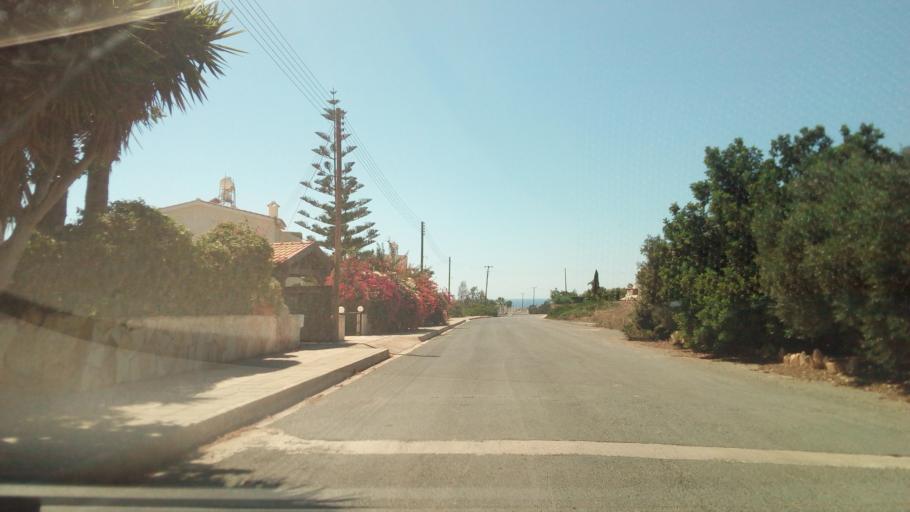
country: CY
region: Pafos
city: Pegeia
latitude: 34.8882
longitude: 32.3343
